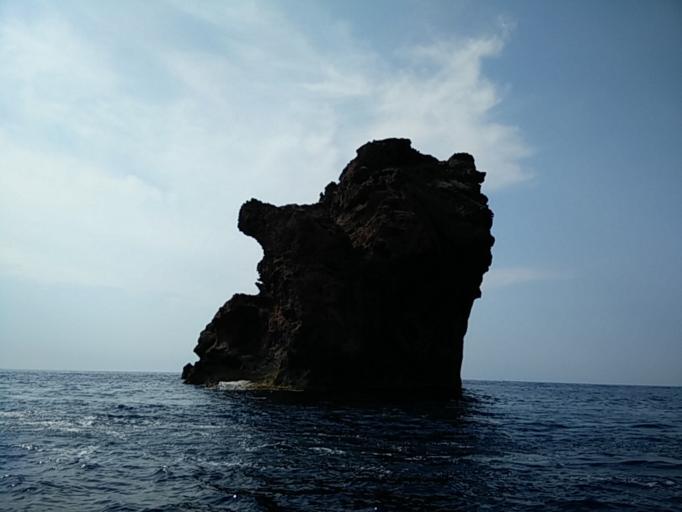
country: FR
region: Corsica
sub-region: Departement de la Corse-du-Sud
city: Cargese
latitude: 42.3798
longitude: 8.5476
